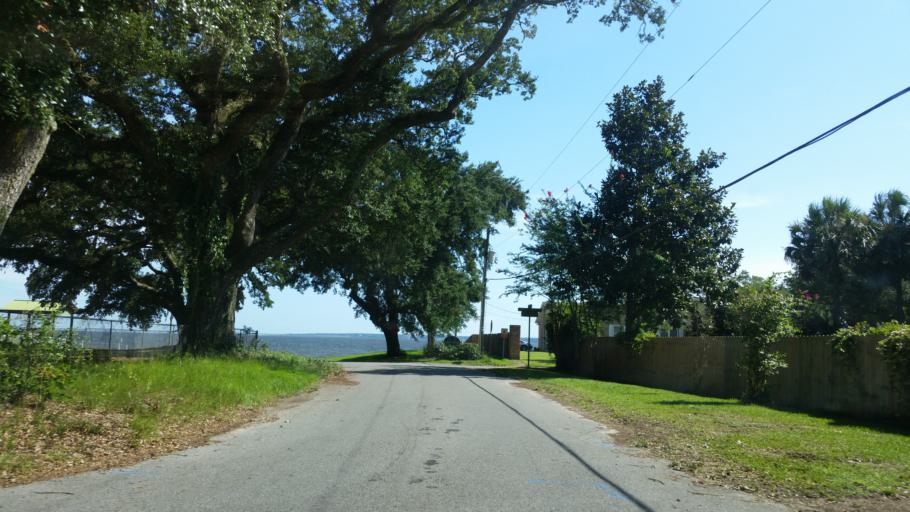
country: US
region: Florida
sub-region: Santa Rosa County
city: Pace
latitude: 30.5820
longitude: -87.1616
